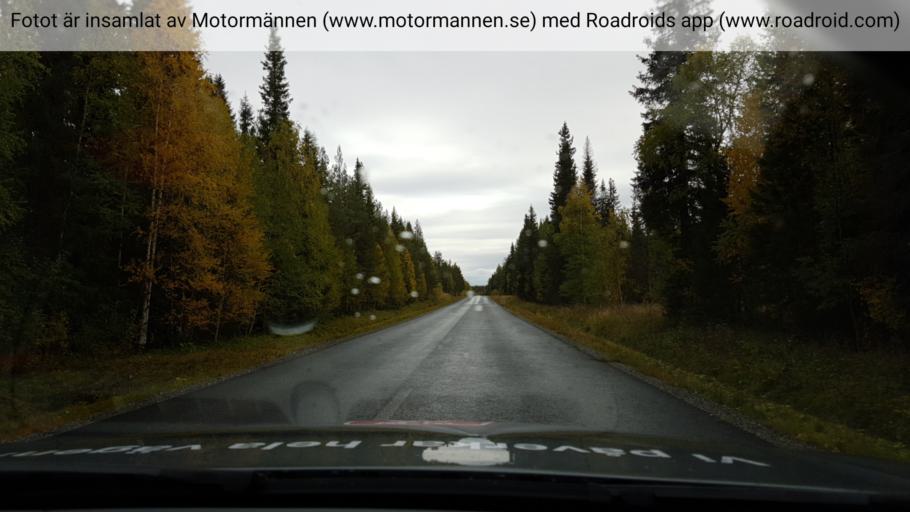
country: SE
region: Vaesterbotten
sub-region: Vilhelmina Kommun
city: Sjoberg
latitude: 64.7129
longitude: 16.2433
